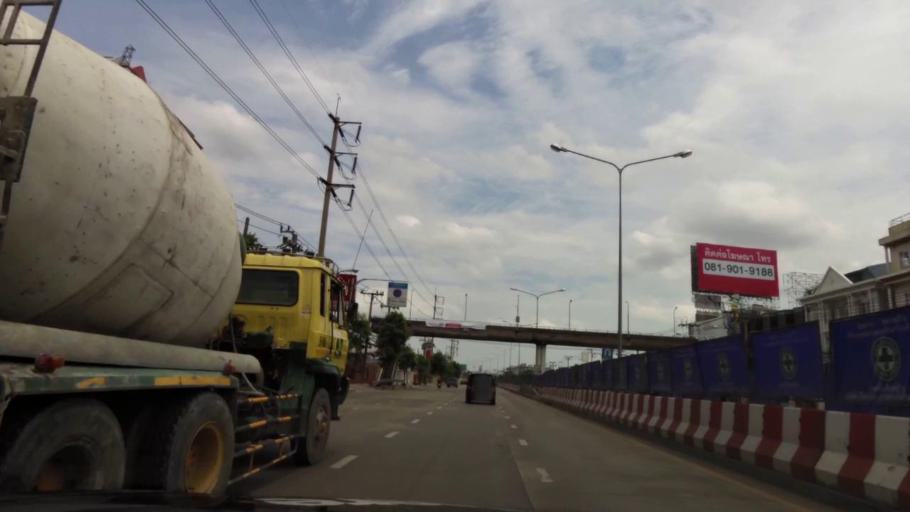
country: TH
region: Bangkok
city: Suan Luang
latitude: 13.7214
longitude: 100.6421
